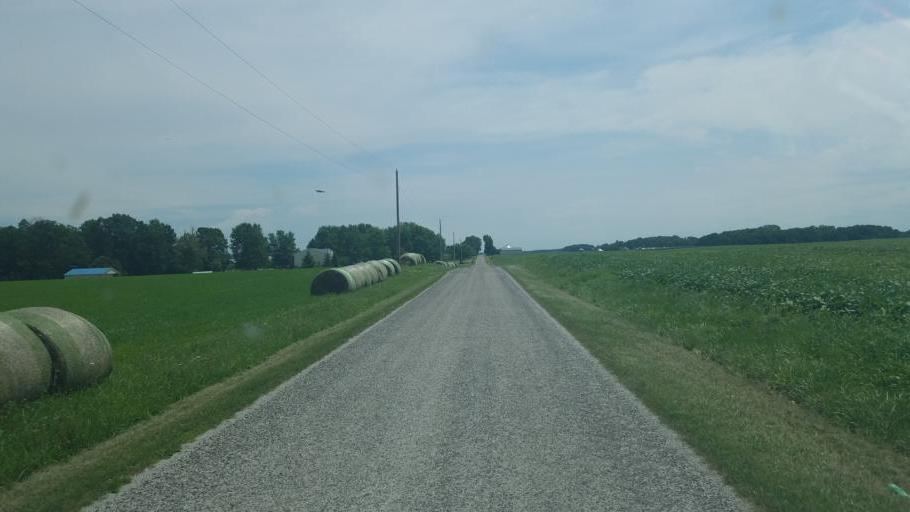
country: US
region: Ohio
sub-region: Crawford County
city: Bucyrus
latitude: 40.8740
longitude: -82.9383
